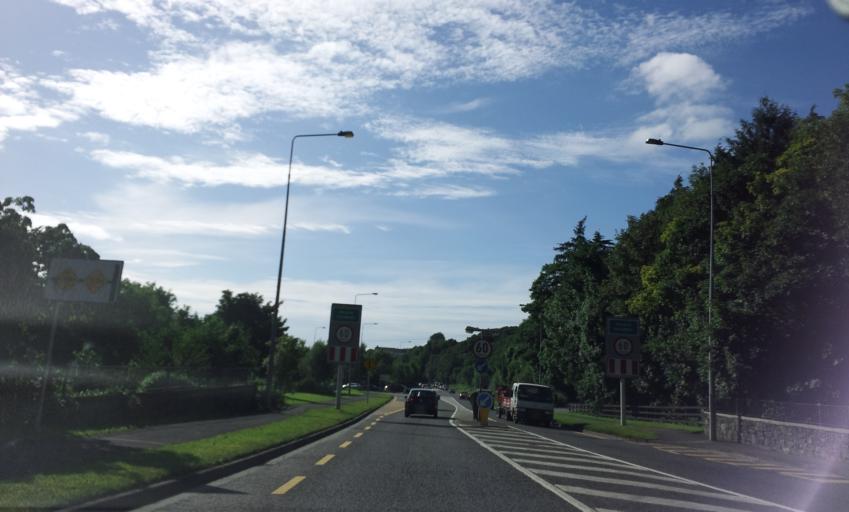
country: IE
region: Munster
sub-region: Ciarrai
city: Cill Airne
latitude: 52.0573
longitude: -9.4691
